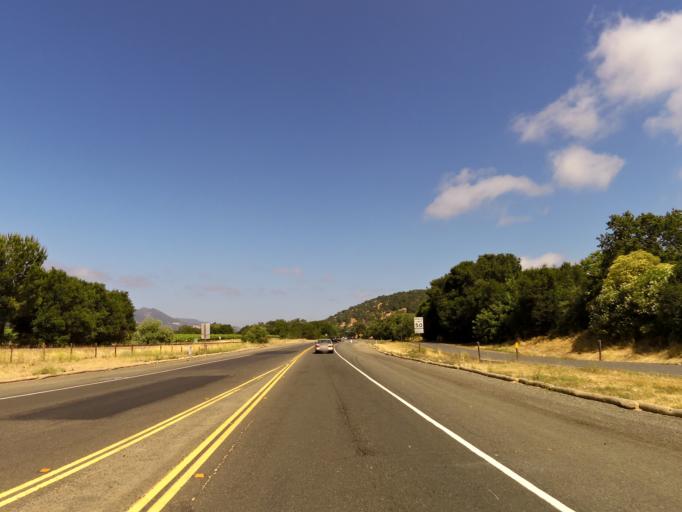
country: US
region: California
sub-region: Napa County
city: Yountville
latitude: 38.4025
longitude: -122.3647
